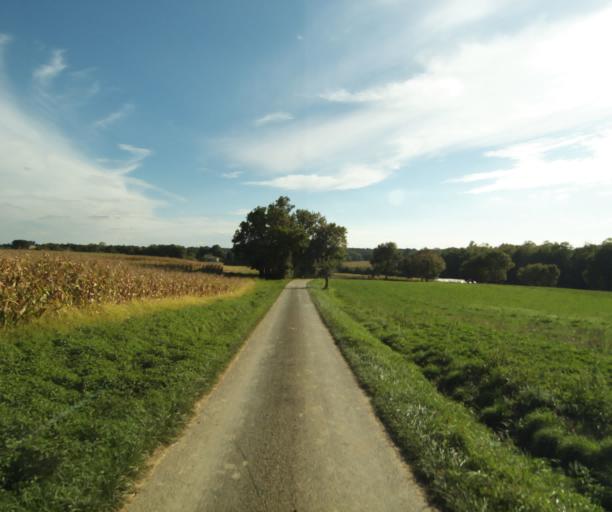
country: FR
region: Midi-Pyrenees
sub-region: Departement du Gers
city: Eauze
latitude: 43.8631
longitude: 0.0407
